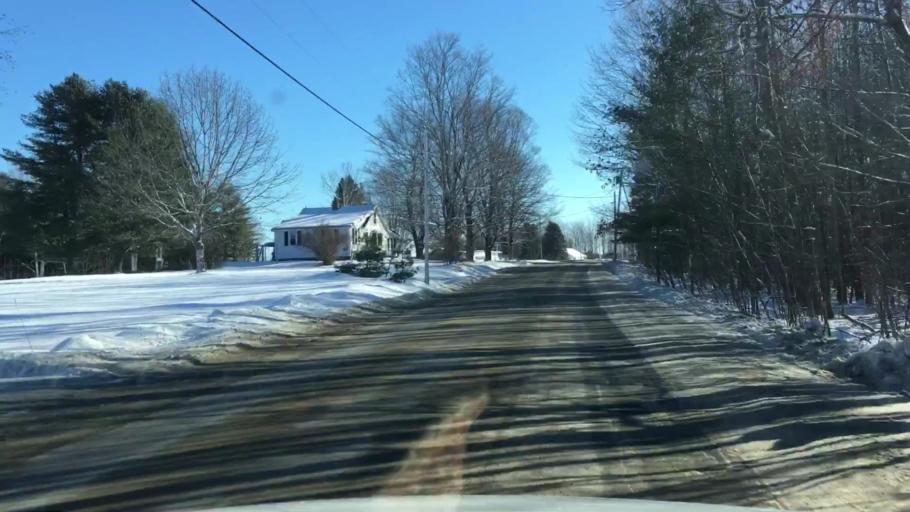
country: US
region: Maine
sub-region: Kennebec County
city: Winthrop
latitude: 44.3342
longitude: -69.9865
